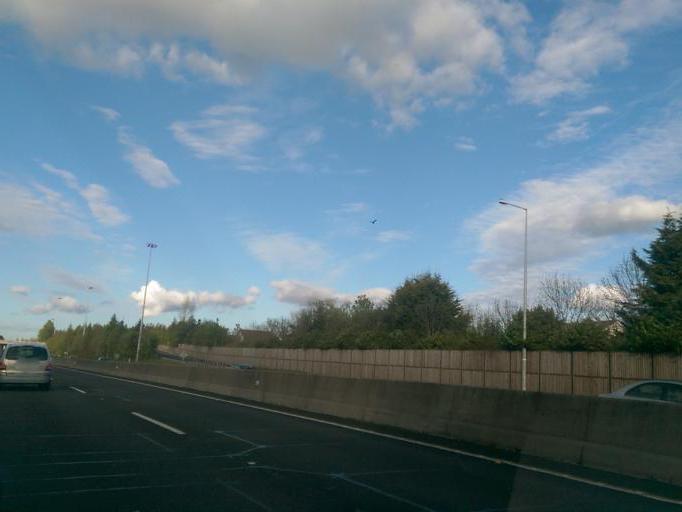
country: IE
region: Leinster
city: Lucan
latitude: 53.3554
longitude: -6.4296
